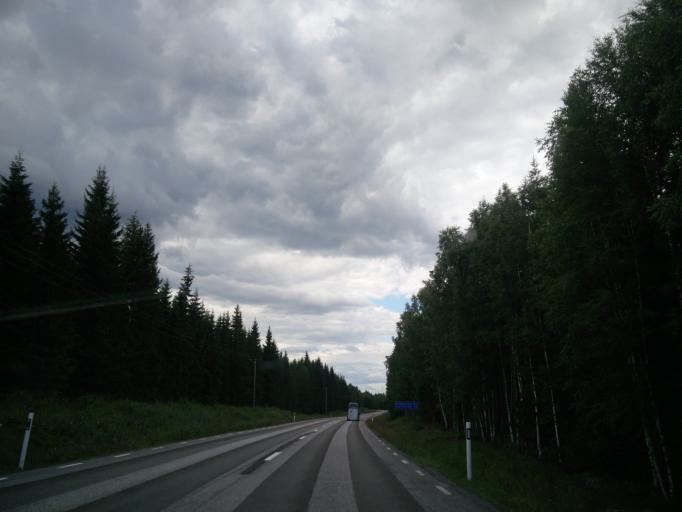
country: SE
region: OErebro
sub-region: Hallefors Kommun
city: Haellefors
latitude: 59.7767
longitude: 14.3881
